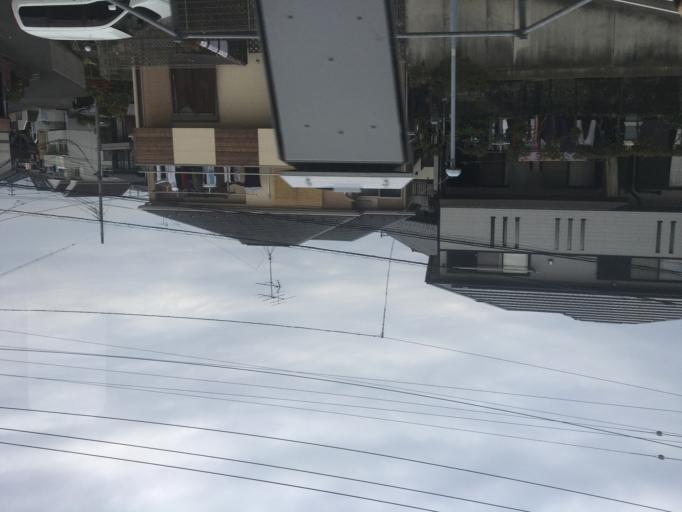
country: JP
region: Saitama
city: Hanno
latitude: 35.8444
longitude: 139.3321
